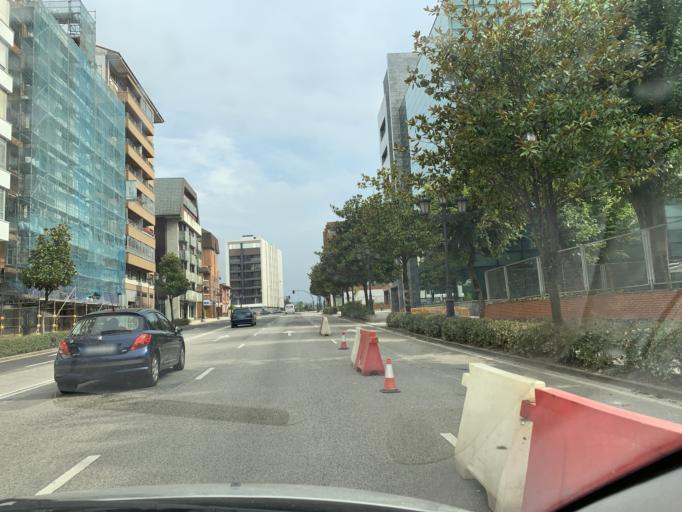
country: ES
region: Asturias
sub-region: Province of Asturias
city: Oviedo
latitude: 43.3580
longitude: -5.8576
